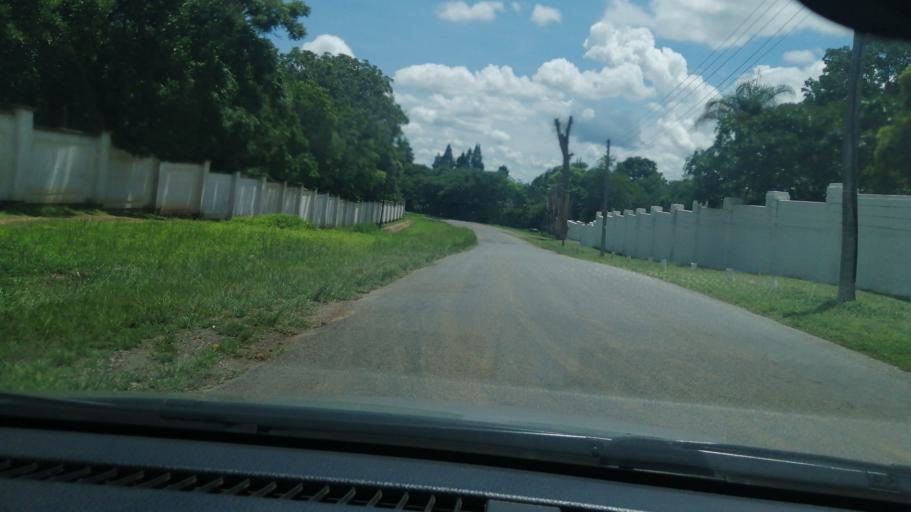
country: ZW
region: Harare
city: Harare
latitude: -17.7727
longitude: 31.0957
